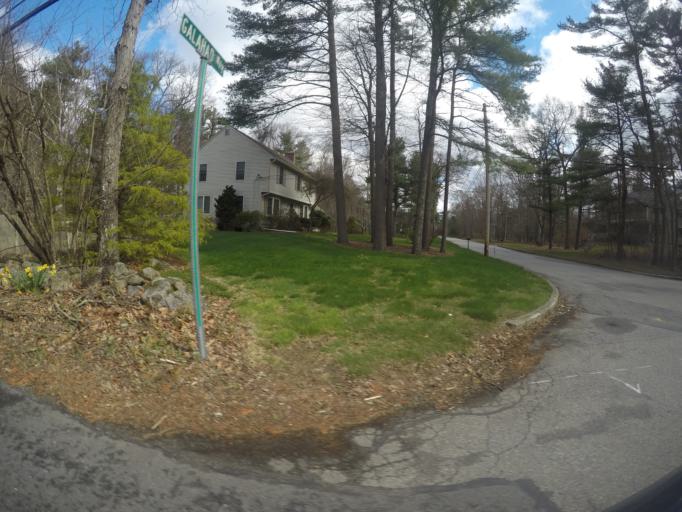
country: US
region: Massachusetts
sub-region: Bristol County
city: Easton
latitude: 42.0331
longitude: -71.1299
